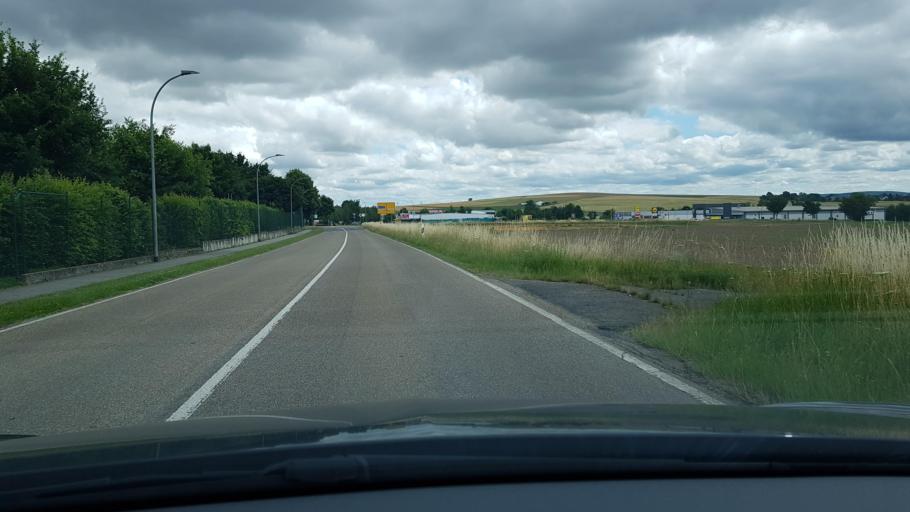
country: DE
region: Rheinland-Pfalz
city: Polch
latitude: 50.3041
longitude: 7.3230
